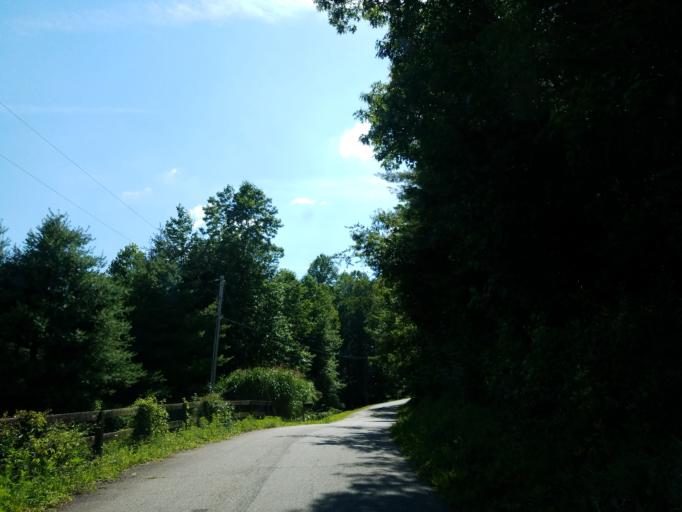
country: US
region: Georgia
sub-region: Dawson County
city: Dawsonville
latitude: 34.5701
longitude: -84.1671
